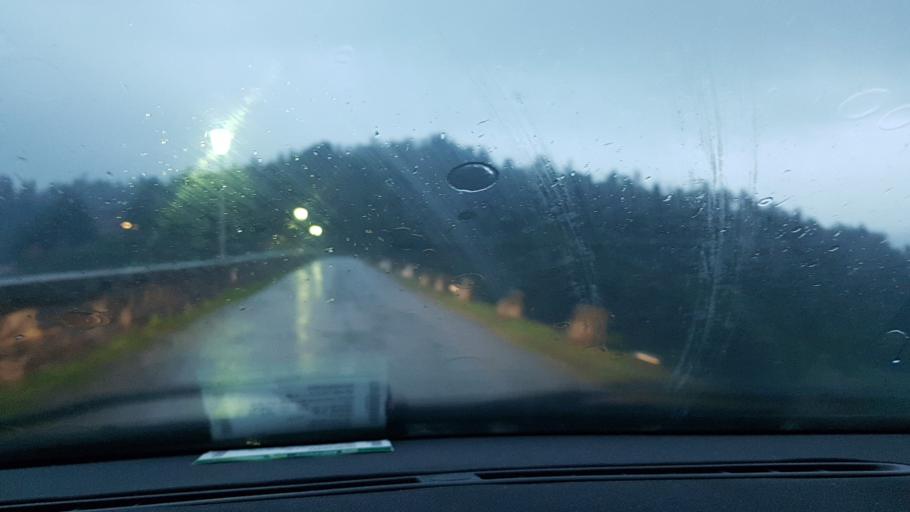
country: HR
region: Primorsko-Goranska
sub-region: Grad Delnice
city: Delnice
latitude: 45.3588
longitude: 14.7202
